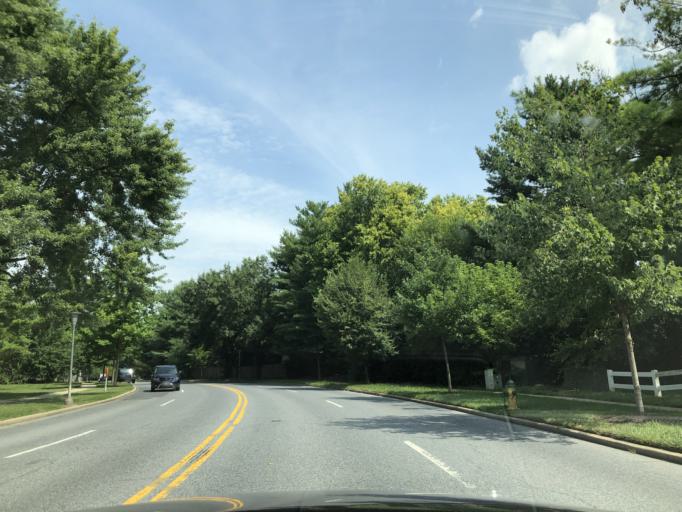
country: US
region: Maryland
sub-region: Frederick County
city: Clover Hill
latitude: 39.4246
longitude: -77.4478
